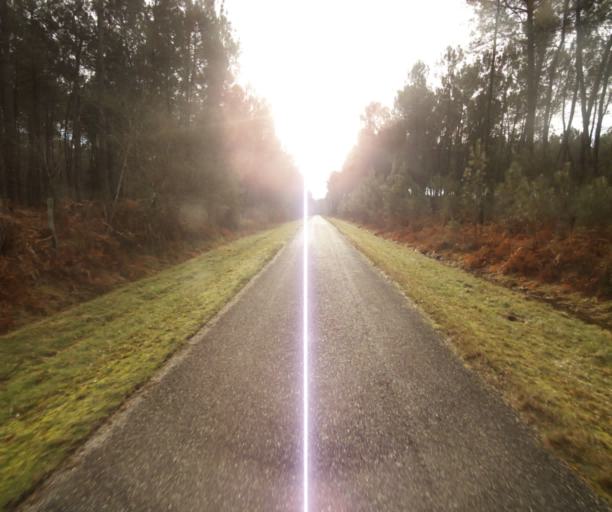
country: FR
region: Aquitaine
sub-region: Departement des Landes
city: Gabarret
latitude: 44.0691
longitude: 0.0904
